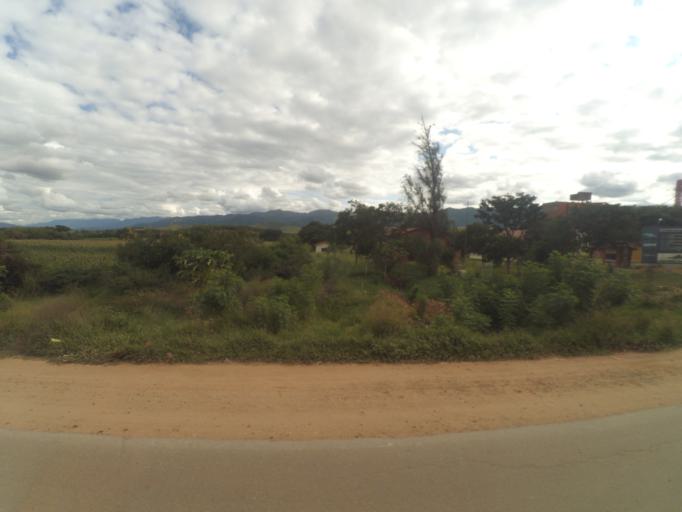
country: BO
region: Santa Cruz
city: Samaipata
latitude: -18.1629
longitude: -63.9188
